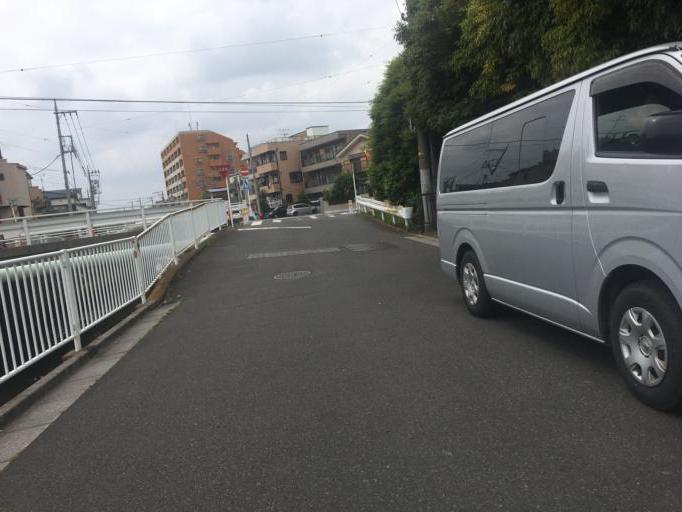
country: JP
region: Saitama
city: Kawaguchi
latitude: 35.8277
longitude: 139.7126
